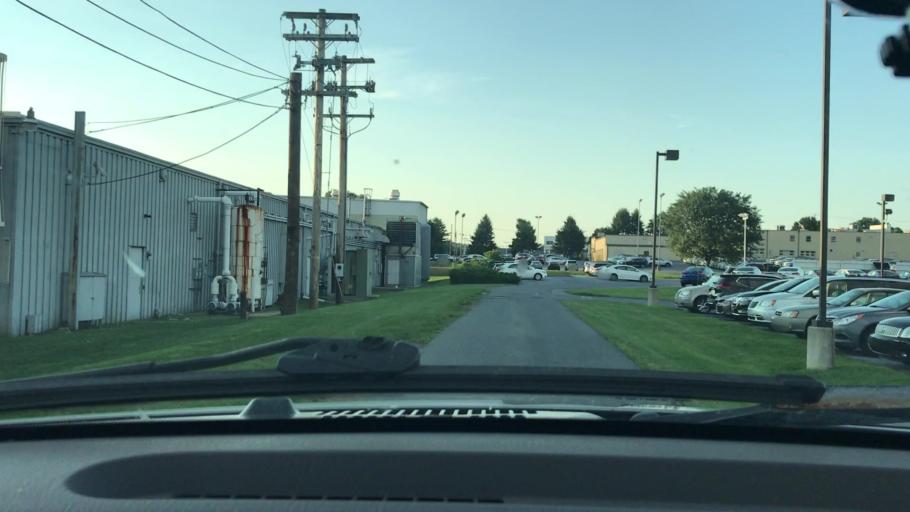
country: US
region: Pennsylvania
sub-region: Lancaster County
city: East Petersburg
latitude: 40.0869
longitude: -76.3472
